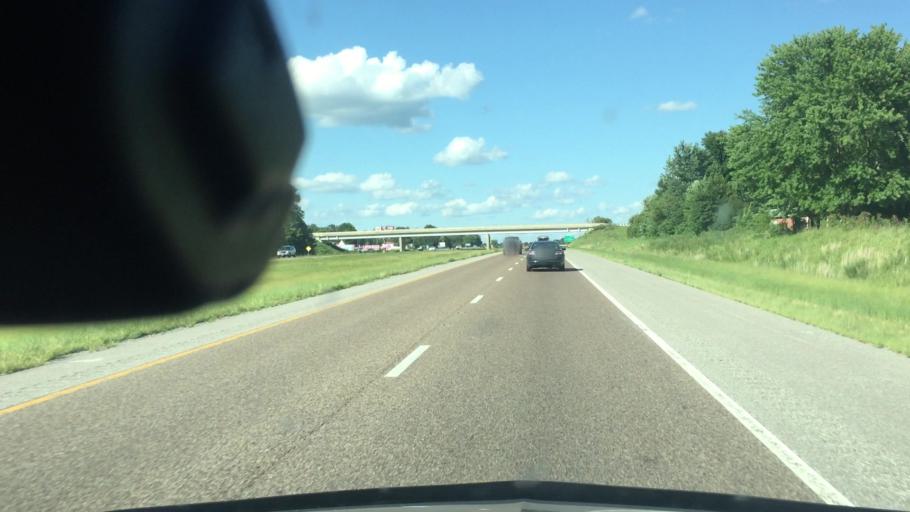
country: US
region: Illinois
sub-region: Macoupin County
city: Staunton
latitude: 38.9564
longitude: -89.7679
